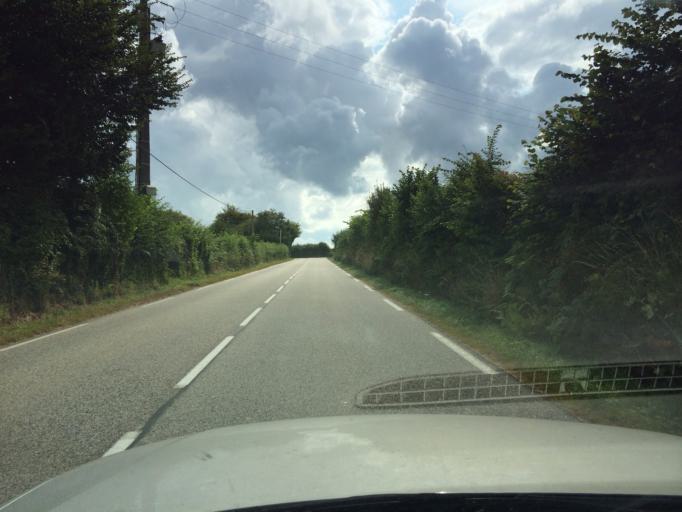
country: FR
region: Lower Normandy
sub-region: Departement de la Manche
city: Brix
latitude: 49.5631
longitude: -1.5997
